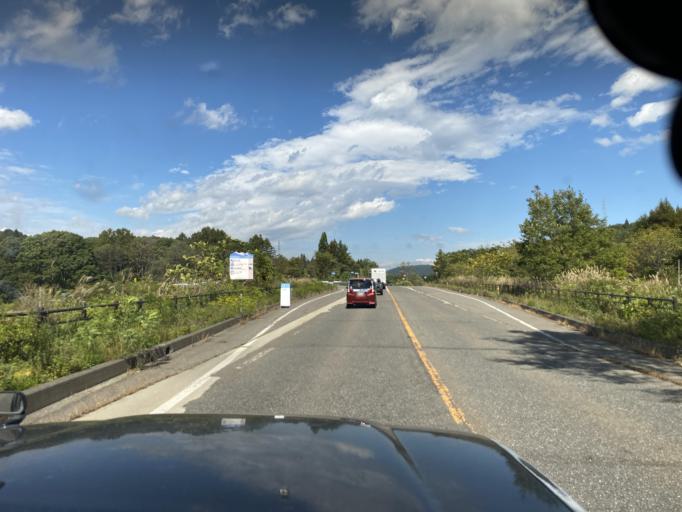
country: JP
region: Nagano
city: Omachi
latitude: 36.5975
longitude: 137.8467
